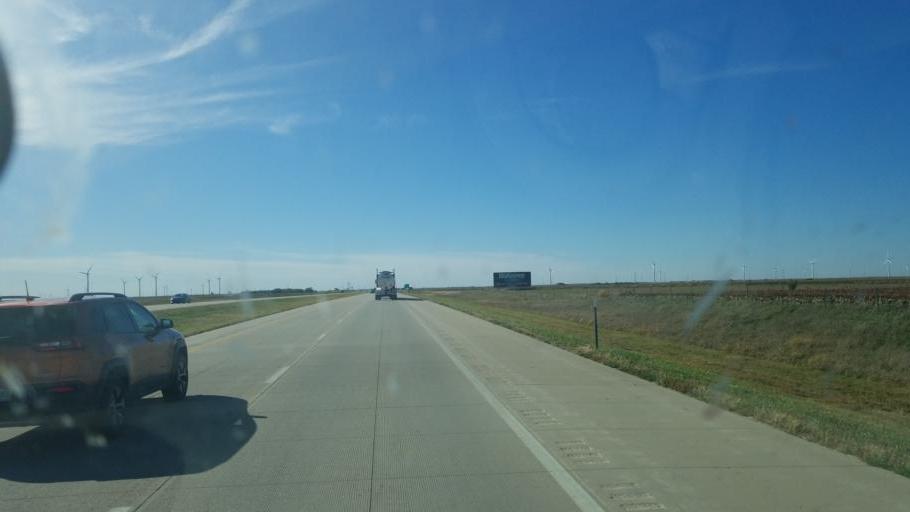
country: US
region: Kansas
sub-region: Ellsworth County
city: Ellsworth
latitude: 38.8495
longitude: -98.2502
